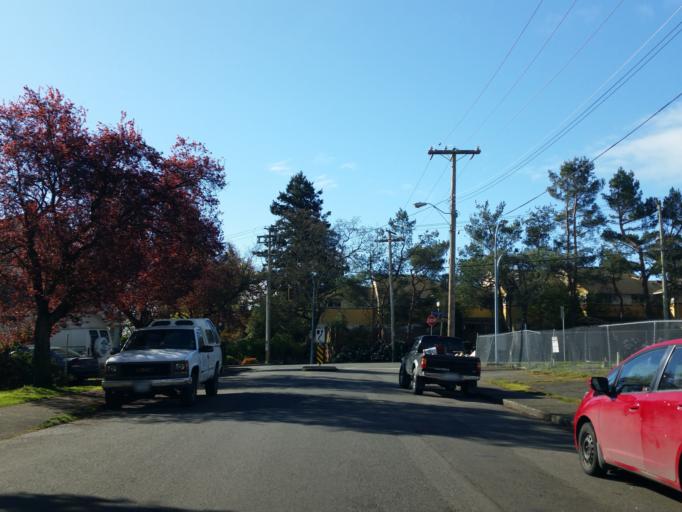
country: CA
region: British Columbia
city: Victoria
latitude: 48.4320
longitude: -123.3935
